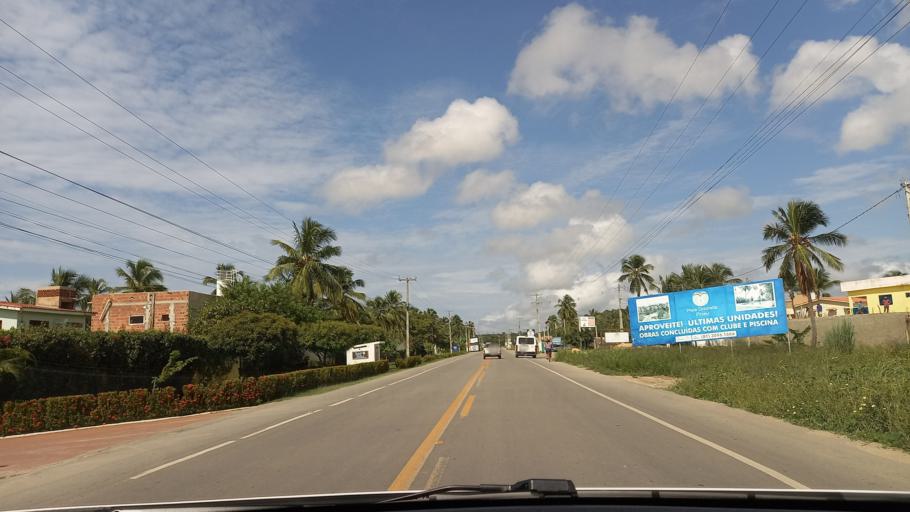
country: BR
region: Pernambuco
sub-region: Sao Jose Da Coroa Grande
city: Sao Jose da Coroa Grande
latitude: -8.9374
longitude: -35.1703
